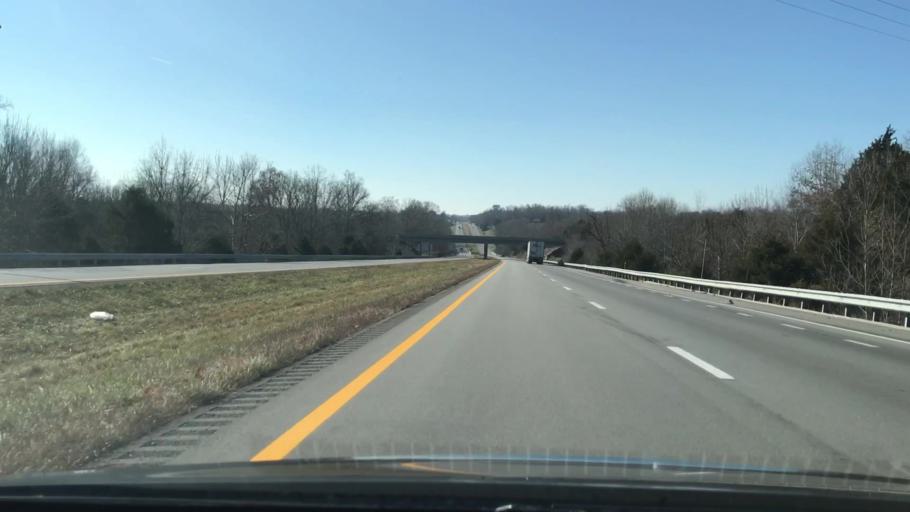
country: US
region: Kentucky
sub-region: Adair County
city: Columbia
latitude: 37.0852
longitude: -85.3088
